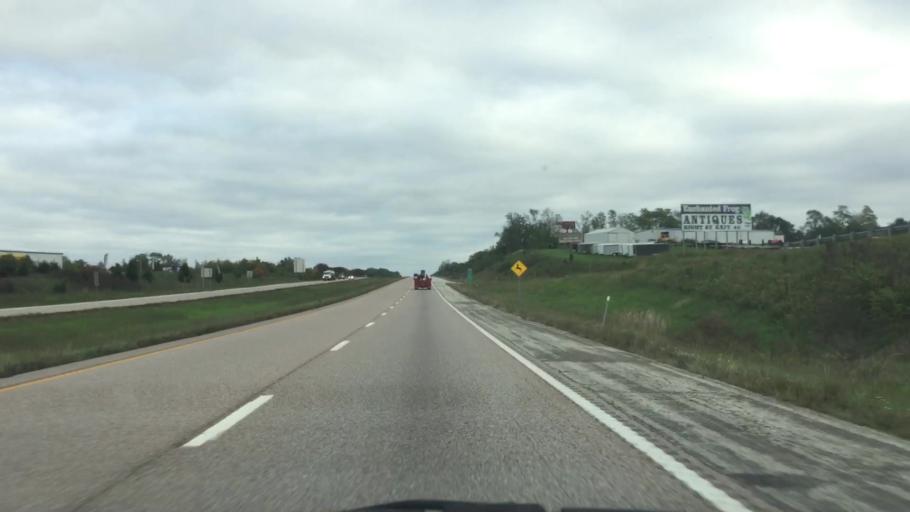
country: US
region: Missouri
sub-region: Clinton County
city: Lathrop
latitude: 39.4606
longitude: -94.3202
